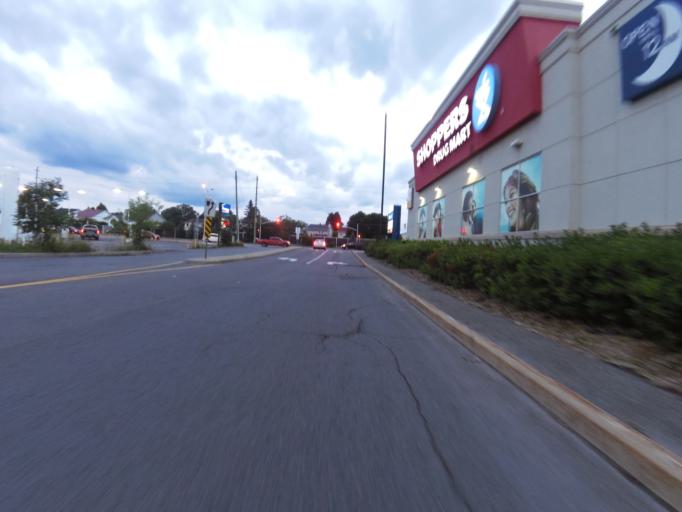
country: CA
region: Ontario
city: Ottawa
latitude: 45.4537
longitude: -75.5080
